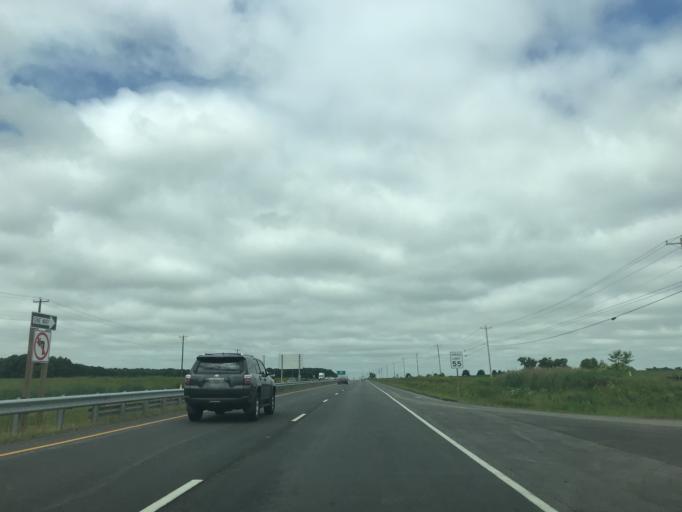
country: US
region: Maryland
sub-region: Caroline County
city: Ridgely
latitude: 38.9259
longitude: -75.9889
